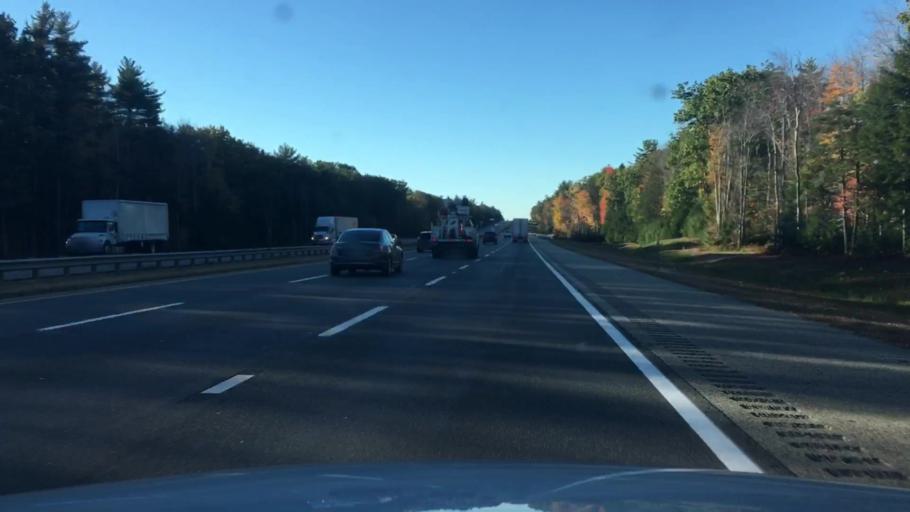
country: US
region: Maine
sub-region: York County
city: Wells Beach Station
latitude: 43.2924
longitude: -70.6166
